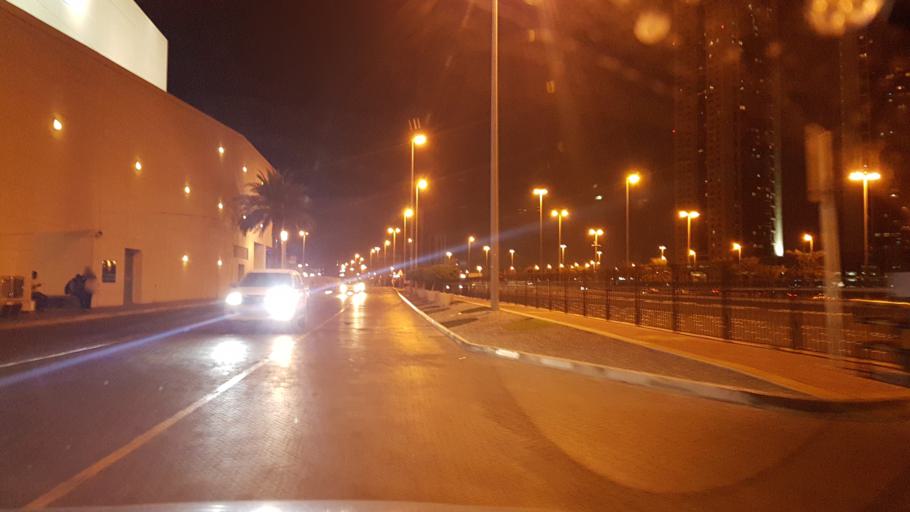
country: BH
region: Manama
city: Jidd Hafs
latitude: 26.2323
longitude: 50.5552
